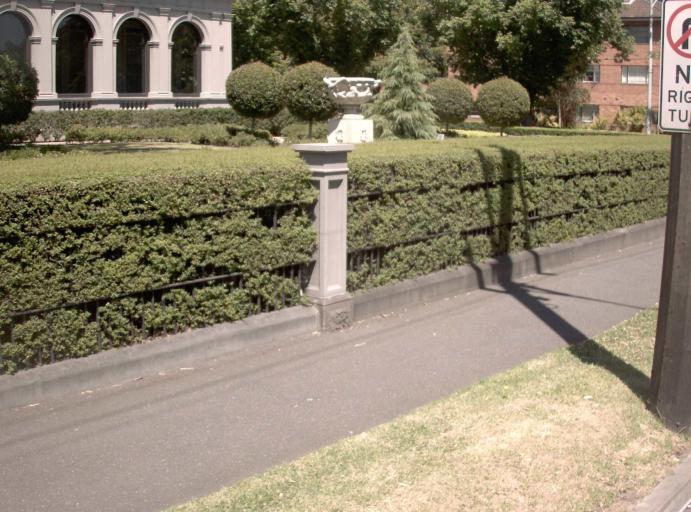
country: AU
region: Victoria
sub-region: Port Phillip
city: St Kilda West
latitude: -37.8478
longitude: 144.9774
